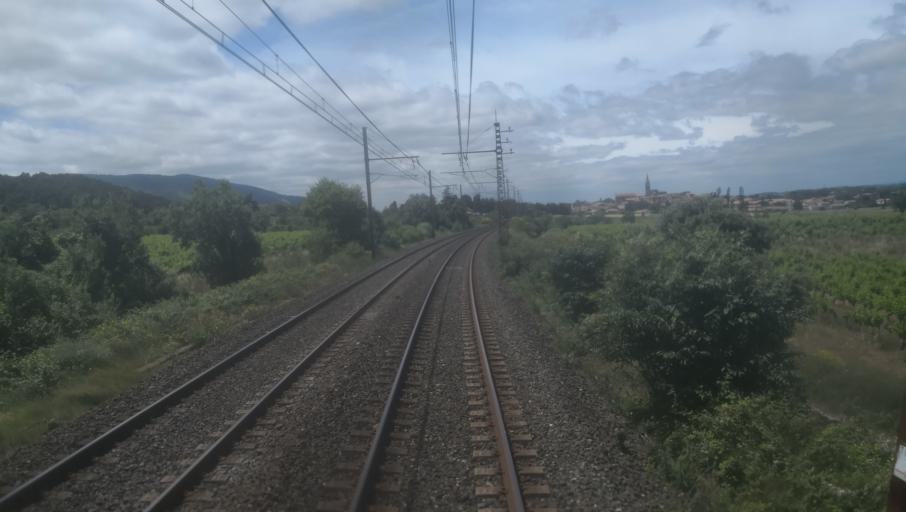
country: FR
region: Languedoc-Roussillon
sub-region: Departement de l'Aude
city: Capendu
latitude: 43.1815
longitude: 2.5707
